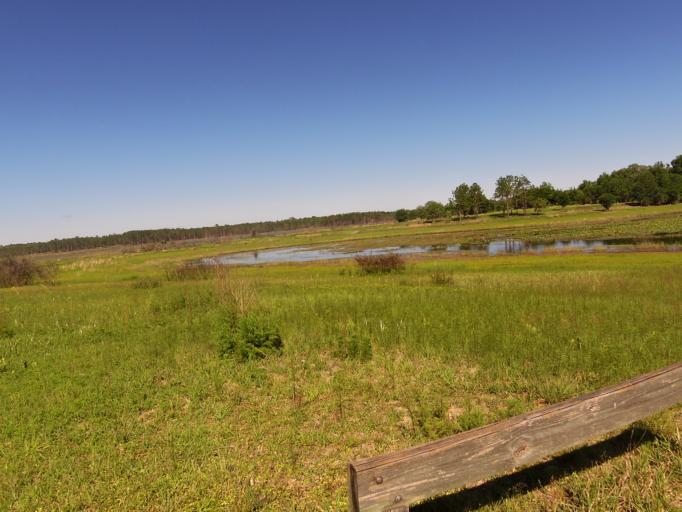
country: US
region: Florida
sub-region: Clay County
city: Keystone Heights
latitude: 29.8224
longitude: -81.9442
